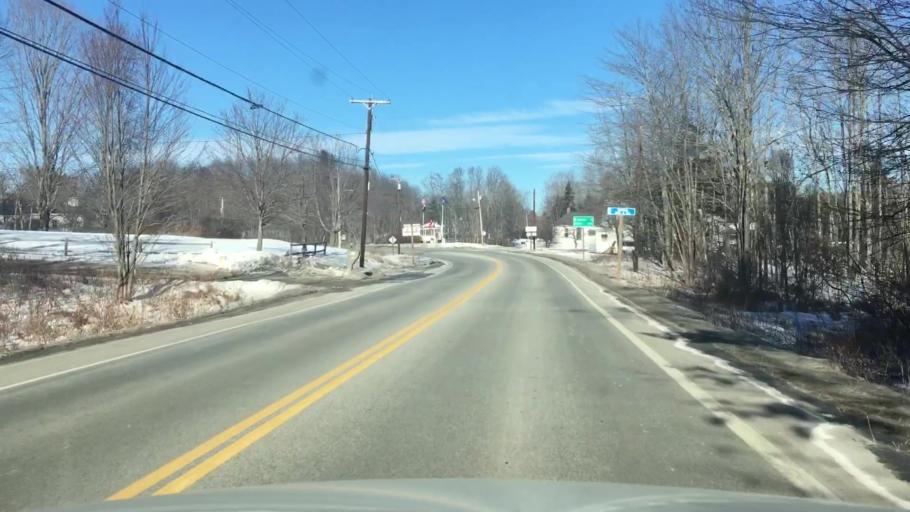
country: US
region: Maine
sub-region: Androscoggin County
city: Lisbon
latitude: 43.9794
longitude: -70.1247
